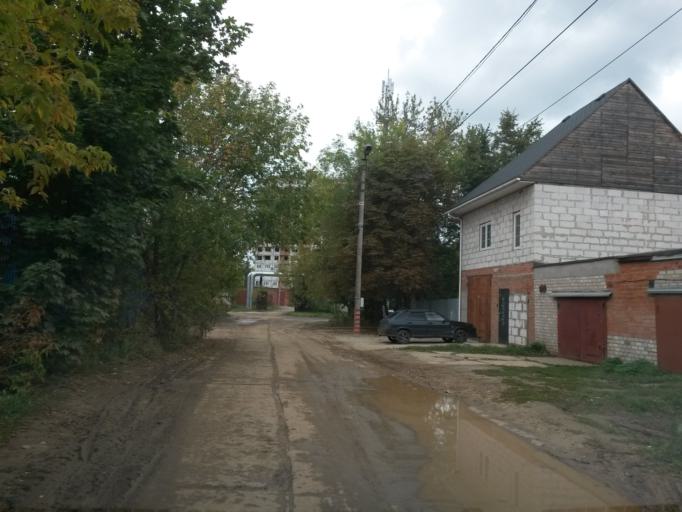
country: RU
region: Moskovskaya
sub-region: Chekhovskiy Rayon
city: Chekhov
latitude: 55.1440
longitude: 37.4798
